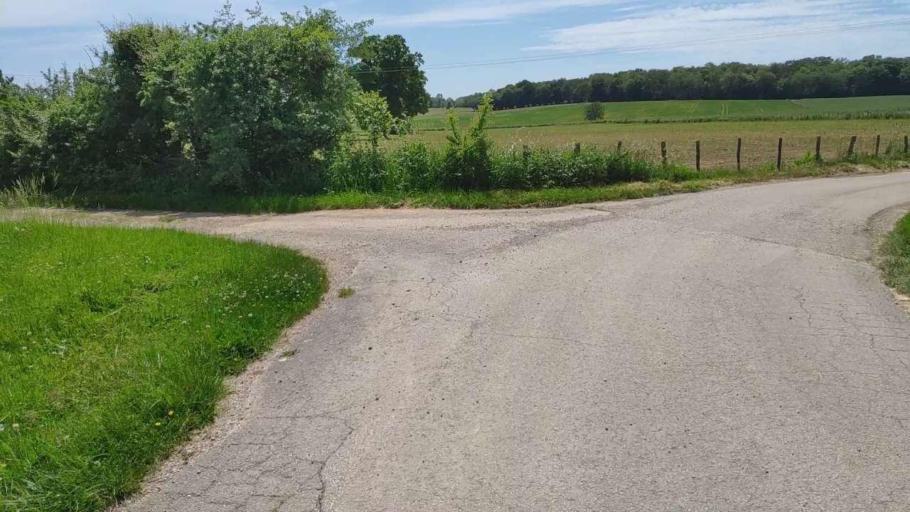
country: FR
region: Franche-Comte
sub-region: Departement du Jura
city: Bletterans
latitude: 46.7610
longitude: 5.4463
